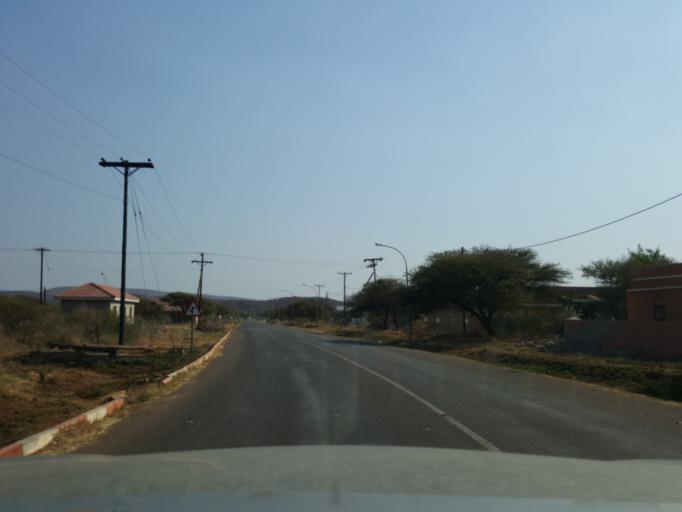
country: BW
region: South East
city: Lobatse
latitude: -25.1931
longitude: 25.6949
